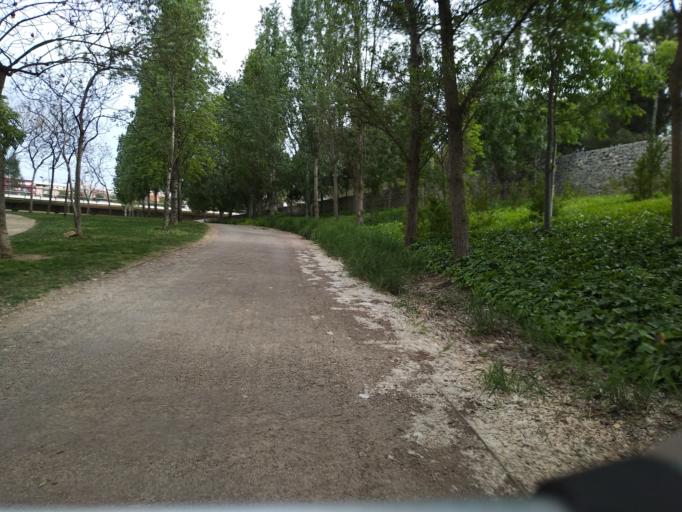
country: ES
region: Valencia
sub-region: Provincia de Valencia
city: Mislata
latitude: 39.4740
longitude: -0.4073
